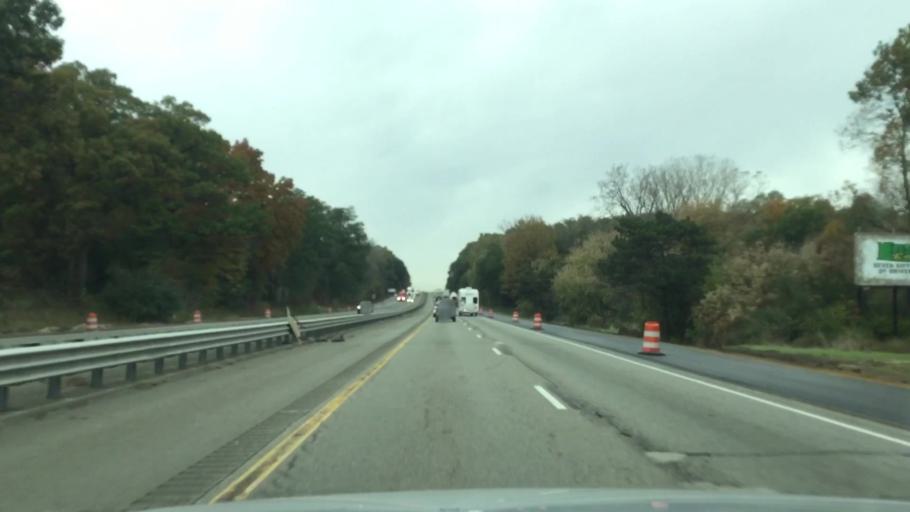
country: US
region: Michigan
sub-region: Jackson County
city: Michigan Center
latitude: 42.2774
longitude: -84.3417
